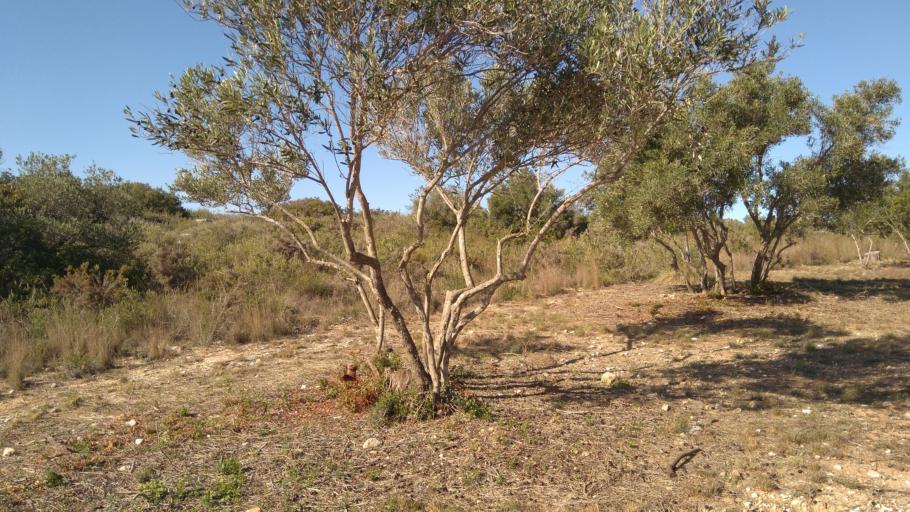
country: ES
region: Valencia
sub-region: Provincia de Valencia
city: Benimodo
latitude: 39.1880
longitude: -0.5695
